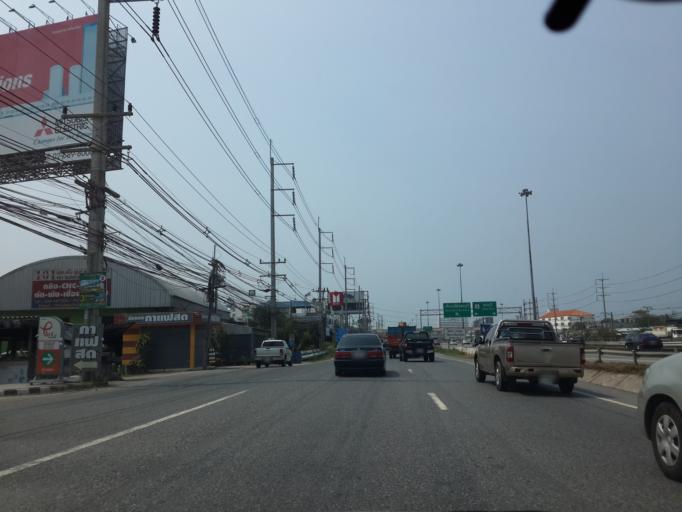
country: TH
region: Chon Buri
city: Chon Buri
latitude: 13.4259
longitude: 101.0019
